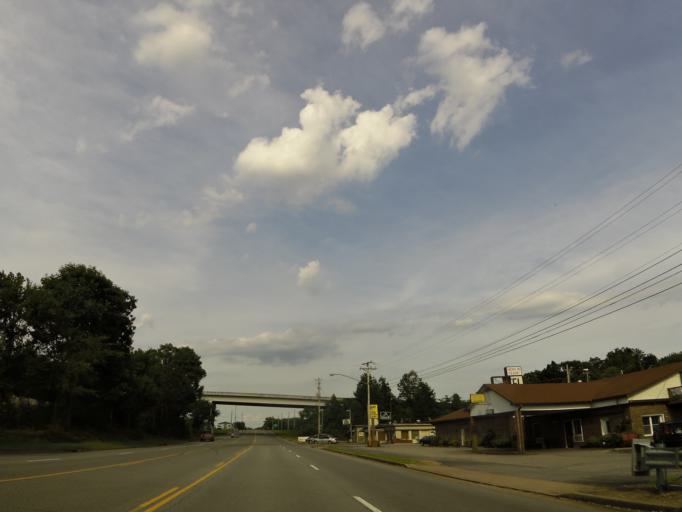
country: US
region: Tennessee
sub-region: Humphreys County
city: New Johnsonville
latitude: 36.0187
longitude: -87.9853
